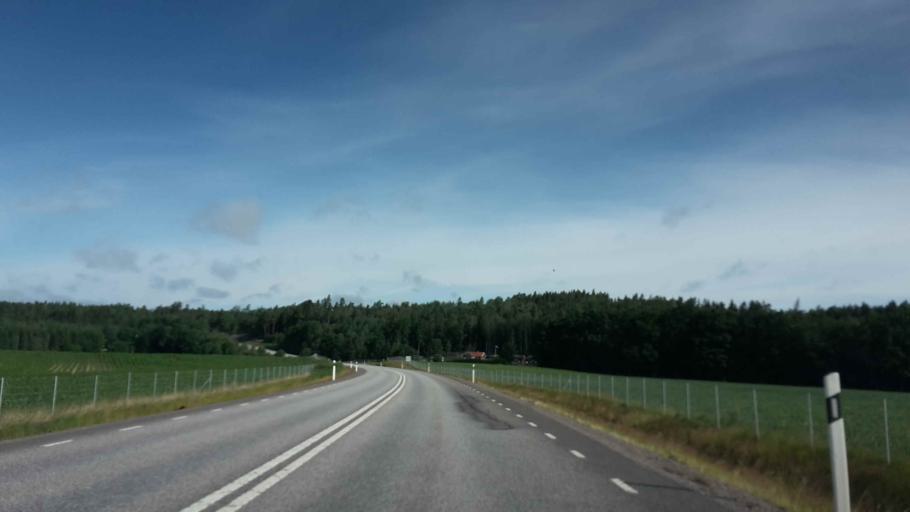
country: SE
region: OEstergoetland
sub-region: Motala Kommun
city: Borensberg
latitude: 58.5567
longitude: 15.3206
